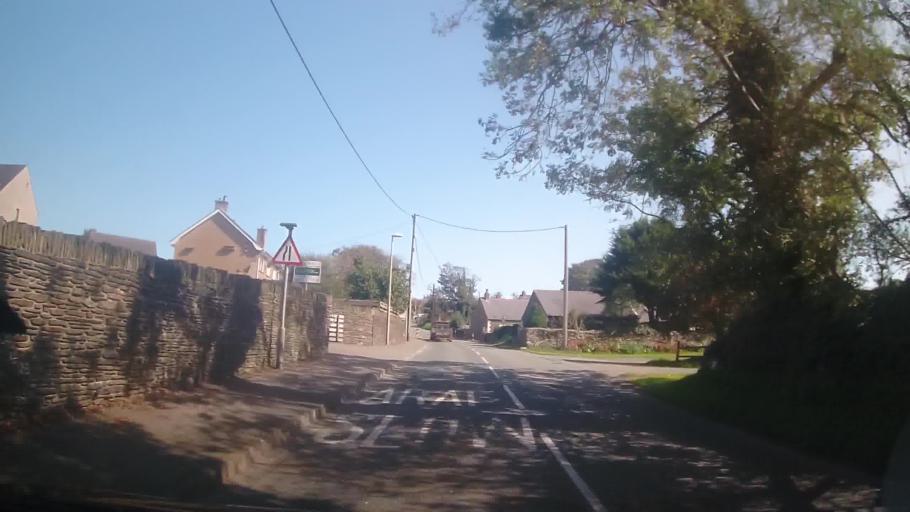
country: GB
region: Wales
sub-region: Pembrokeshire
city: Scleddau
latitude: 51.9269
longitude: -5.0037
